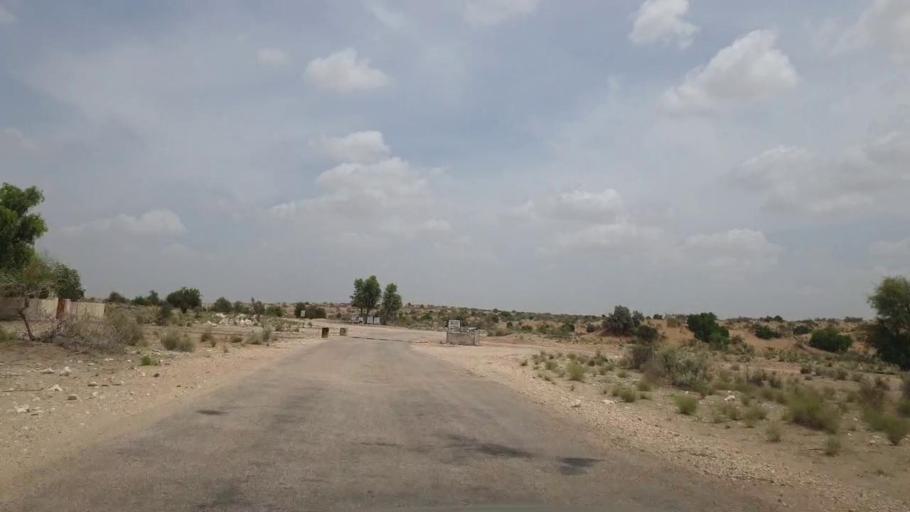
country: PK
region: Sindh
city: Kot Diji
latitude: 27.1658
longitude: 69.2213
